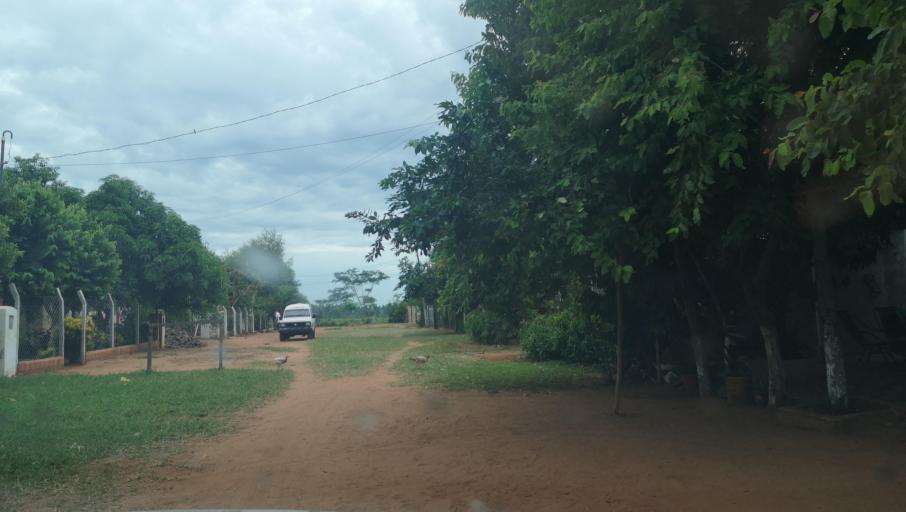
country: PY
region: San Pedro
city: Capiibary
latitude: -24.7423
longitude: -56.0347
